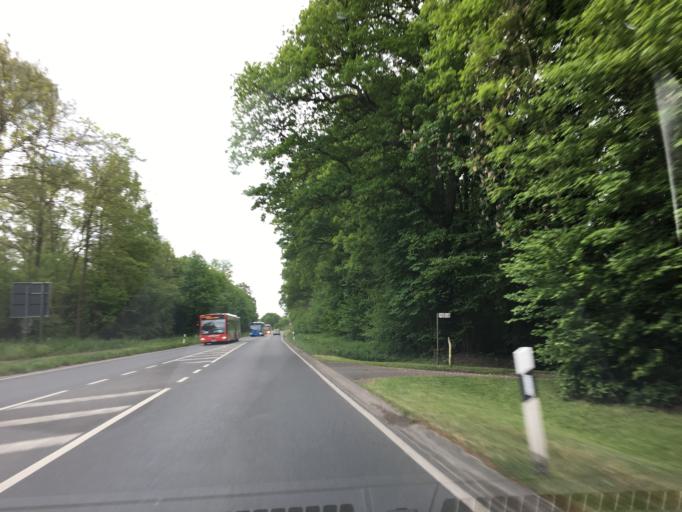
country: DE
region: North Rhine-Westphalia
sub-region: Regierungsbezirk Munster
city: Muenster
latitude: 51.8844
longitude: 7.6479
